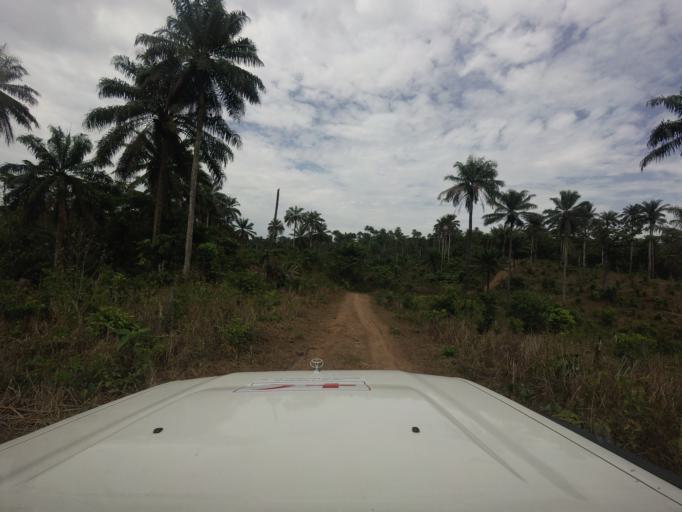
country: SL
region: Eastern Province
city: Buedu
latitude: 8.2449
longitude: -10.2597
